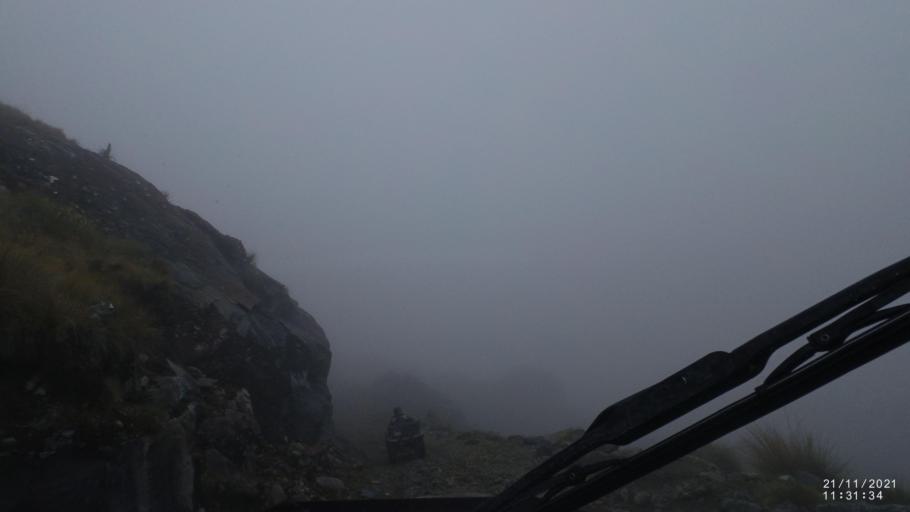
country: BO
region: Cochabamba
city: Cochabamba
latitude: -16.9597
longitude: -66.2666
